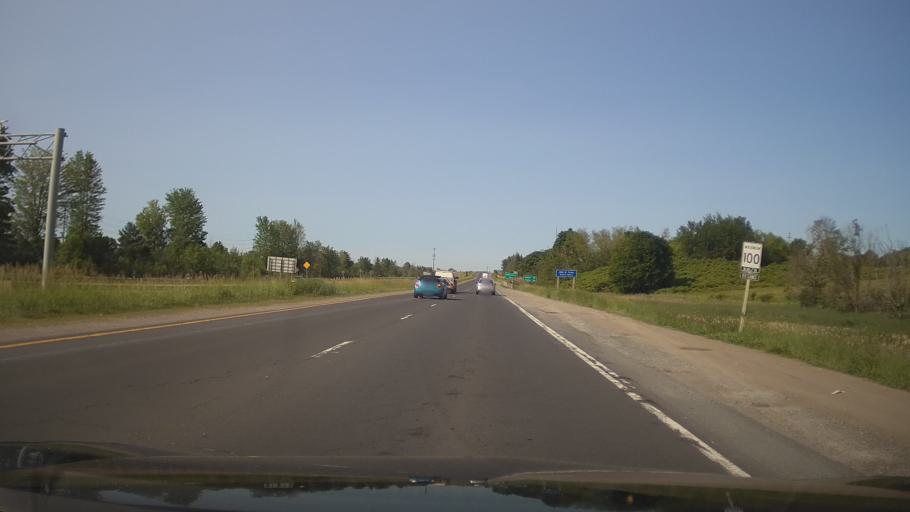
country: CA
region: Ontario
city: Peterborough
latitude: 44.2929
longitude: -78.2838
